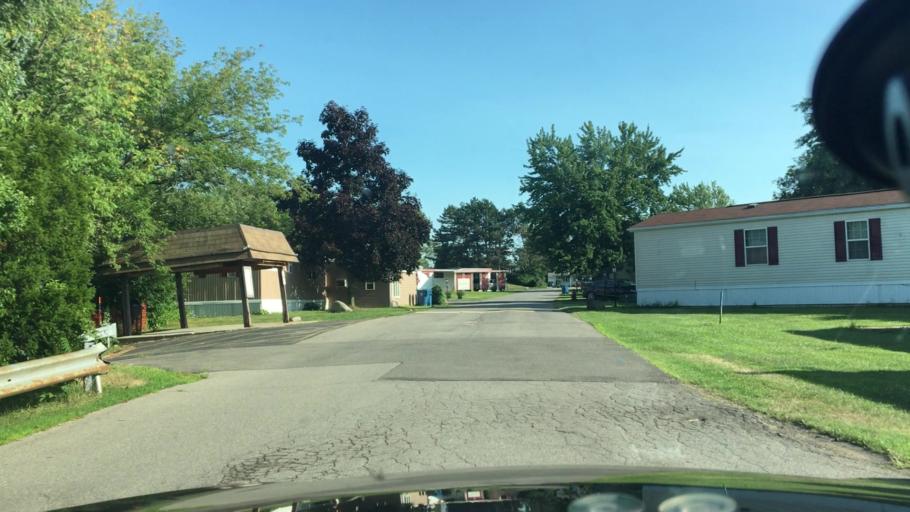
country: US
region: New York
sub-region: Erie County
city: Wanakah
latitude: 42.7603
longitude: -78.8591
